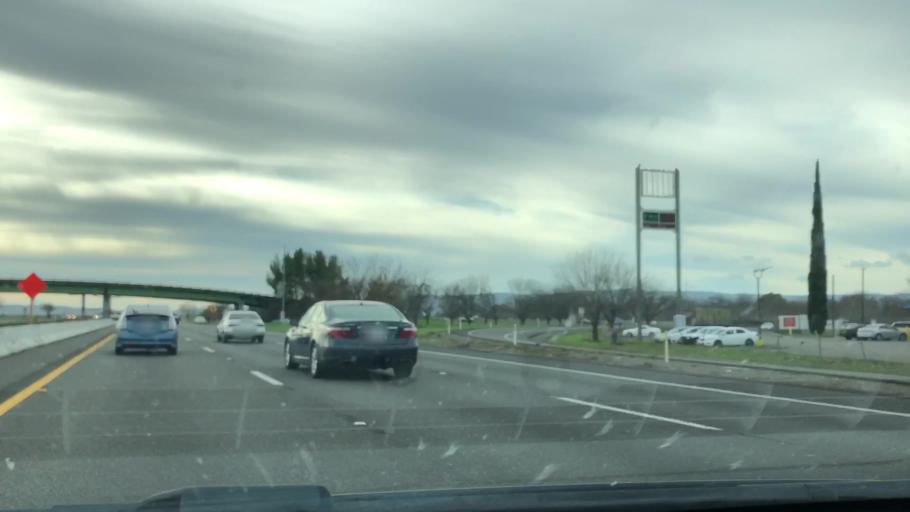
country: US
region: California
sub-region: Solano County
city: Dixon
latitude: 38.4481
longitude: -121.8571
